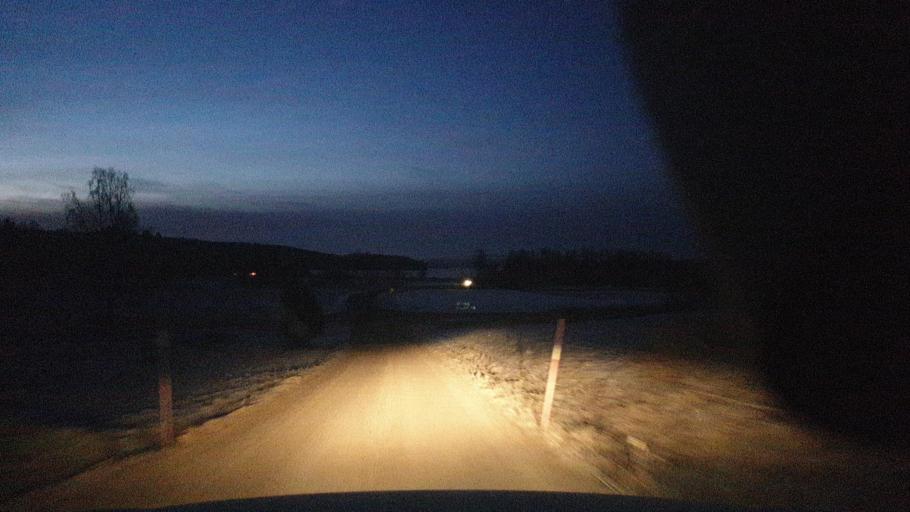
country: SE
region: Vaermland
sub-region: Eda Kommun
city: Amotfors
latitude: 59.8324
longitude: 12.3581
